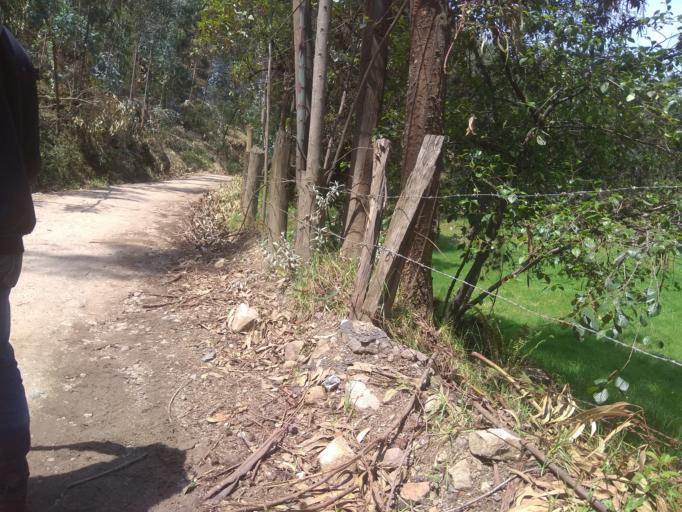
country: CO
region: Boyaca
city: Socha Viejo
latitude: 5.9787
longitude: -72.7234
